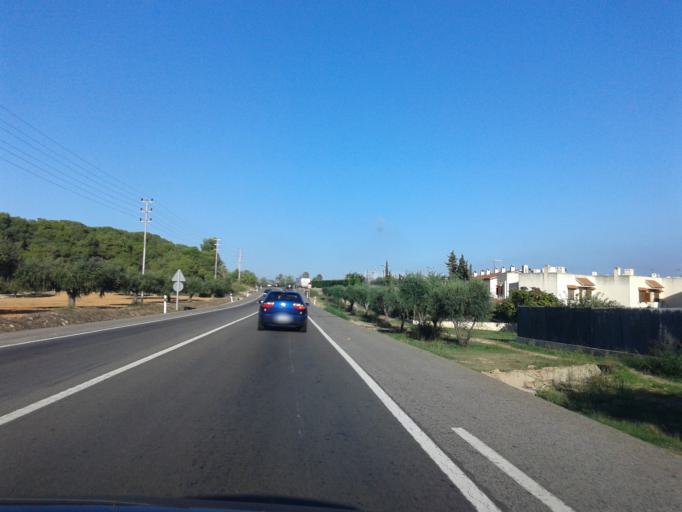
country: ES
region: Catalonia
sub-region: Provincia de Tarragona
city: Roda de Bara
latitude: 41.1685
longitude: 1.4605
